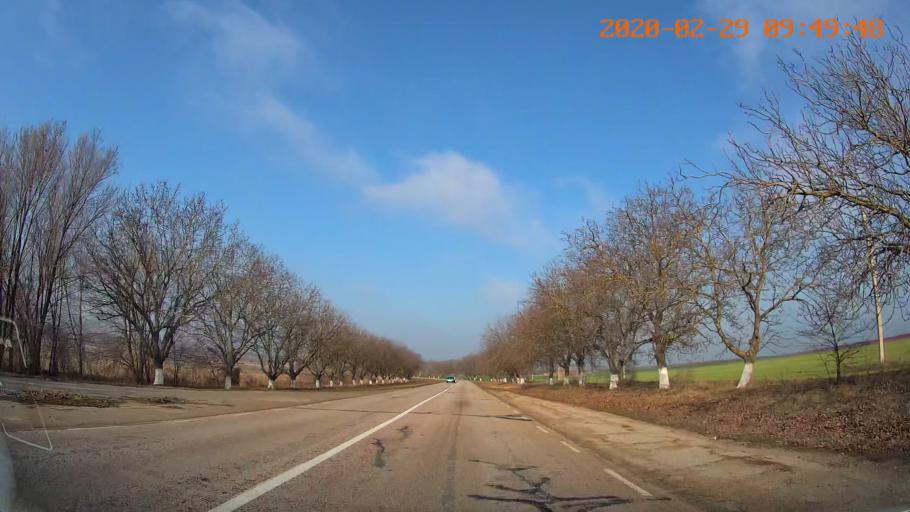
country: MD
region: Telenesti
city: Crasnoe
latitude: 46.6996
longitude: 29.7667
